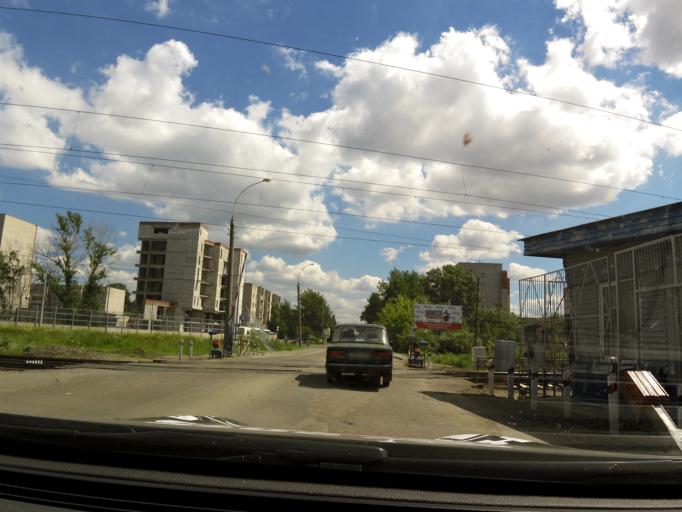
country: RU
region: Vologda
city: Vologda
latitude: 59.2273
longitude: 39.8600
